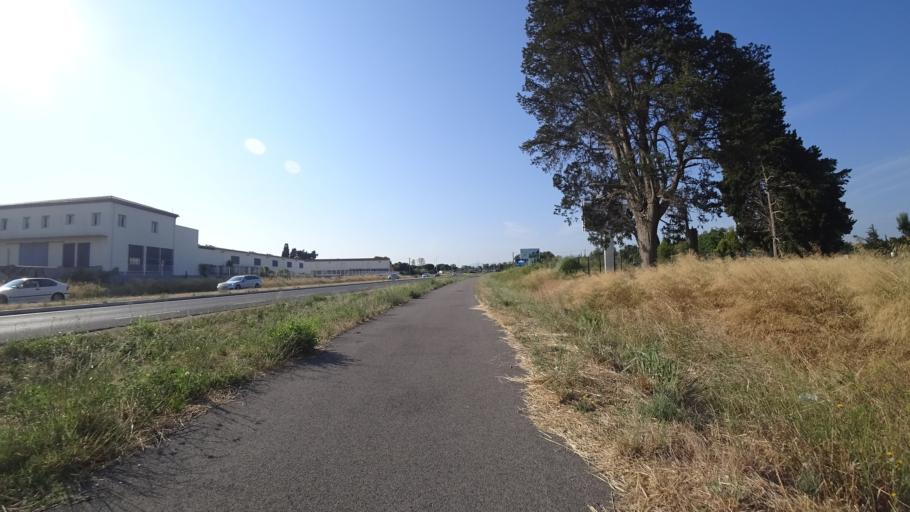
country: FR
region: Languedoc-Roussillon
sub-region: Departement des Pyrenees-Orientales
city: Perpignan
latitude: 42.7116
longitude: 2.9069
